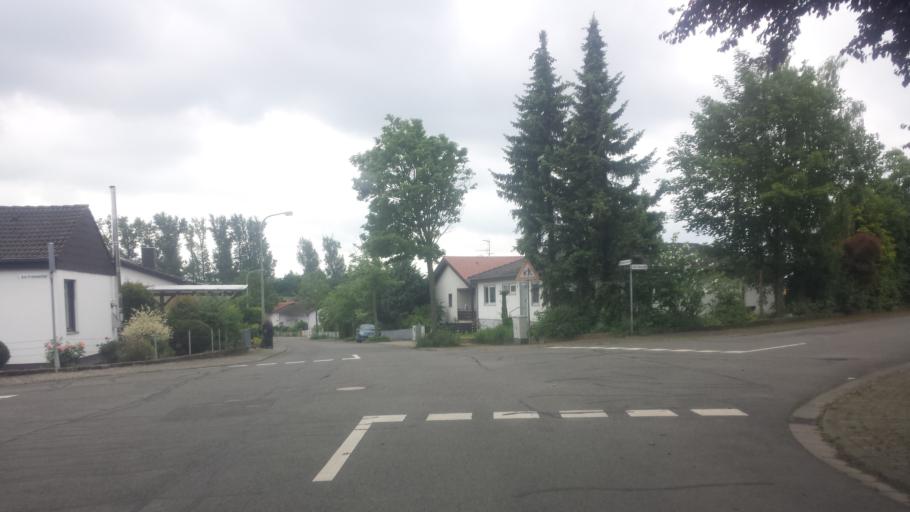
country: DE
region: Rheinland-Pfalz
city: Ilbesheim
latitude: 49.1696
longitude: 8.0714
